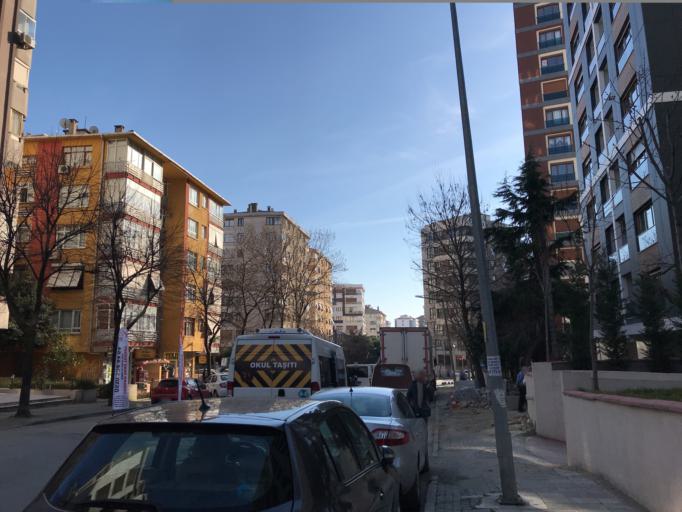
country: TR
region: Istanbul
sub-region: Atasehir
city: Atasehir
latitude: 40.9653
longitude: 29.1016
